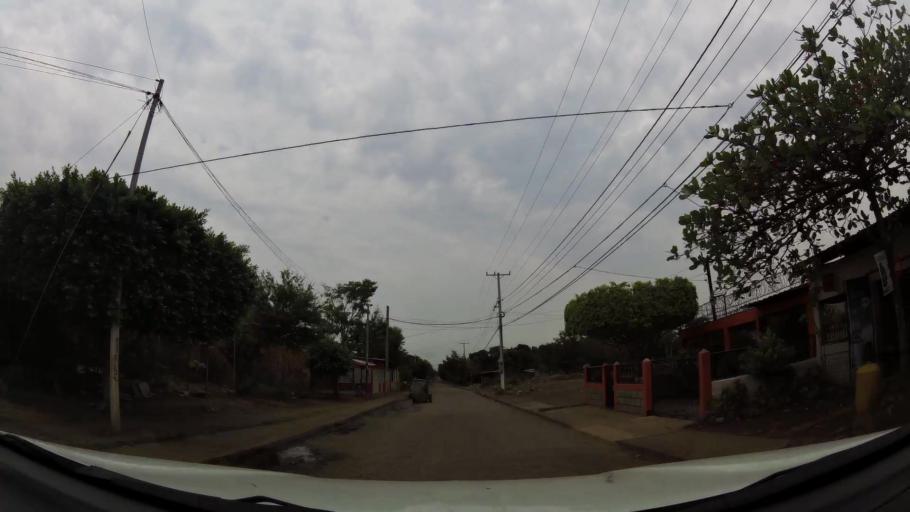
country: NI
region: Granada
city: Granada
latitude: 11.9438
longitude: -85.9525
